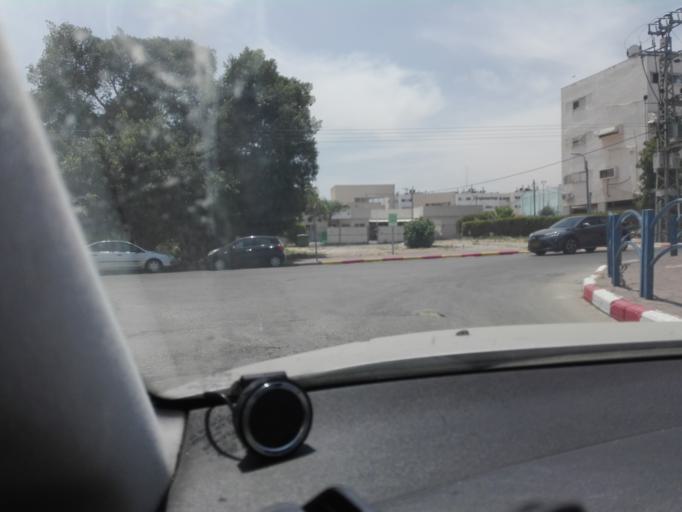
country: IL
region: Central District
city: Bene 'Ayish
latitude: 31.7363
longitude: 34.7414
